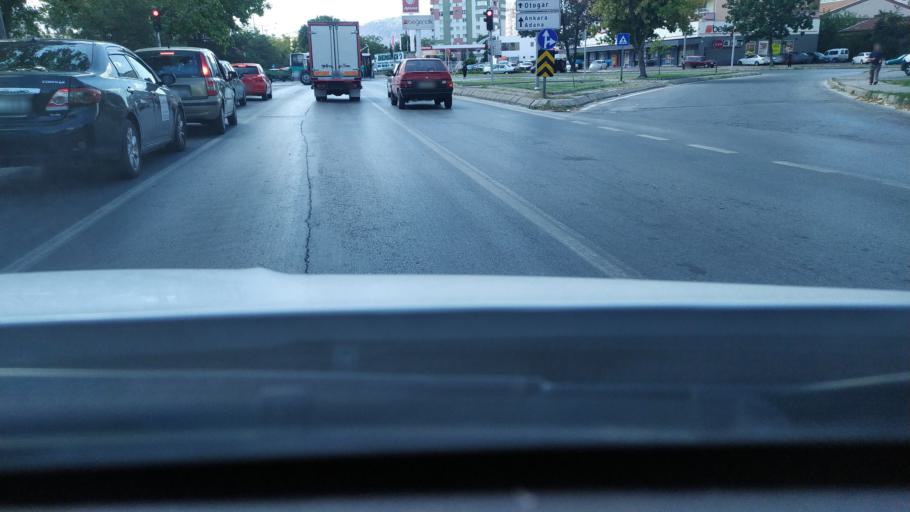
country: TR
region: Kayseri
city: Kayseri
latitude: 38.7149
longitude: 35.4748
